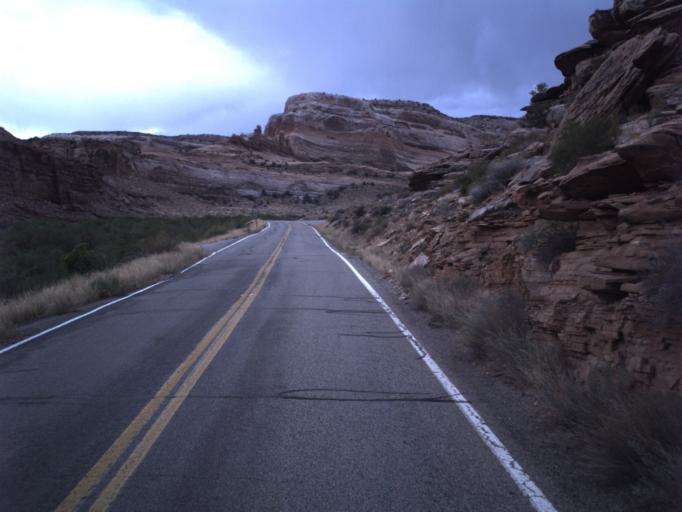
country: US
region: Utah
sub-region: Grand County
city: Moab
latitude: 38.8052
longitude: -109.3130
